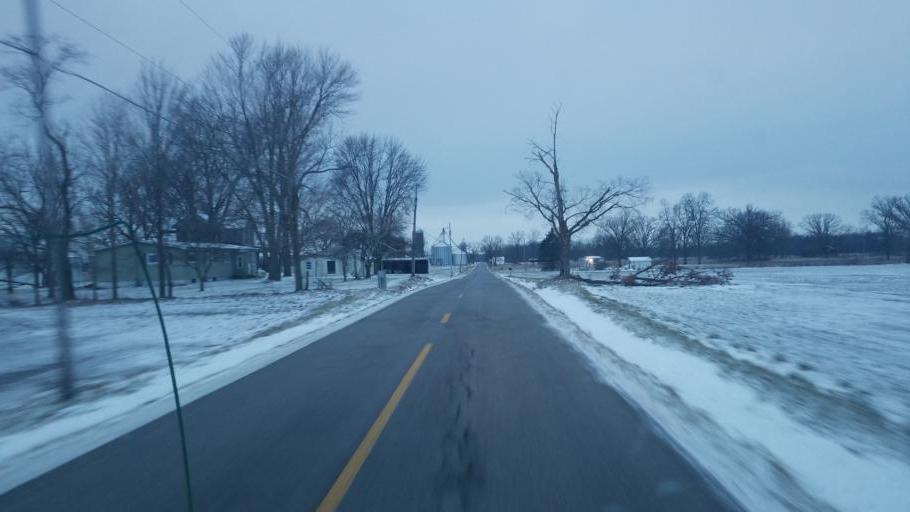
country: US
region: Ohio
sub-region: Delaware County
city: Sunbury
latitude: 40.2045
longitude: -82.8318
